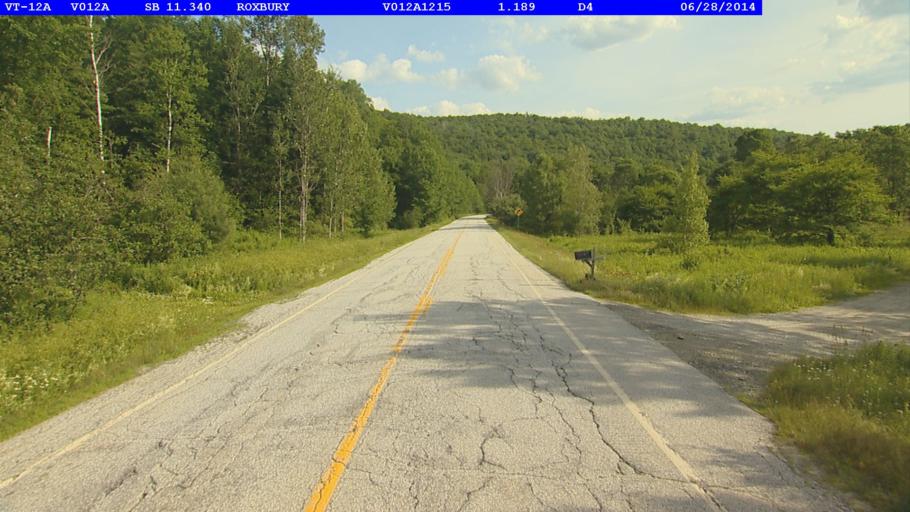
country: US
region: Vermont
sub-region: Washington County
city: Northfield
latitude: 44.0458
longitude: -72.7427
